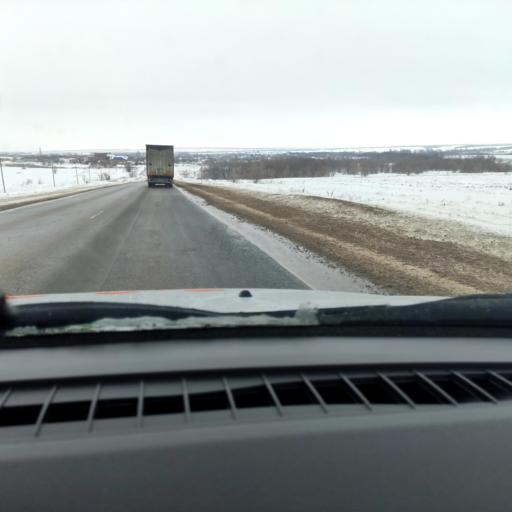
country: RU
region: Samara
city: Dubovyy Umet
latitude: 52.8315
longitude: 50.4929
